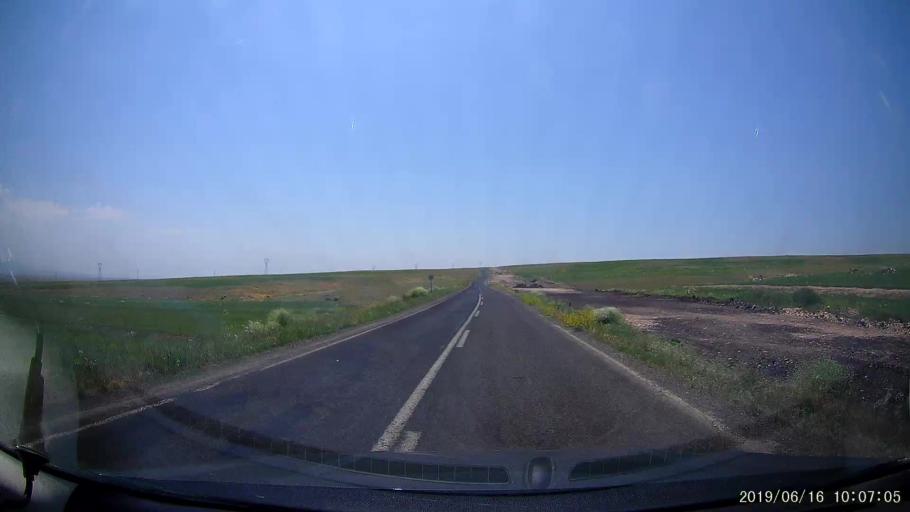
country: TR
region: Kars
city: Digor
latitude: 40.2483
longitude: 43.5510
